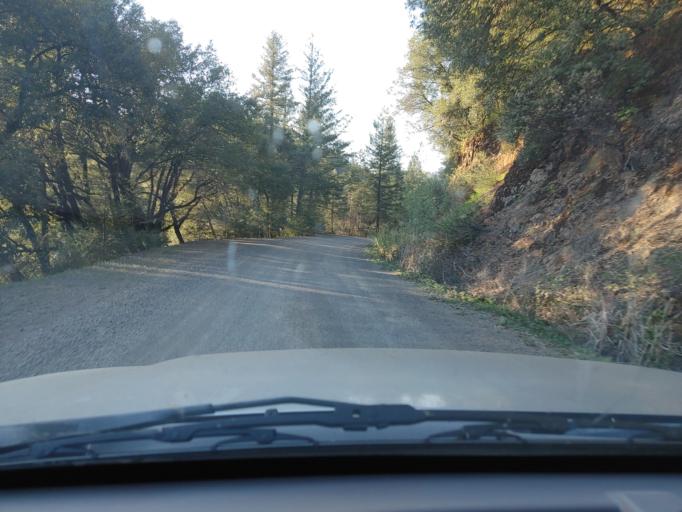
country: US
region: California
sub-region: Shasta County
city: Bella Vista
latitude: 40.8353
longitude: -122.0175
